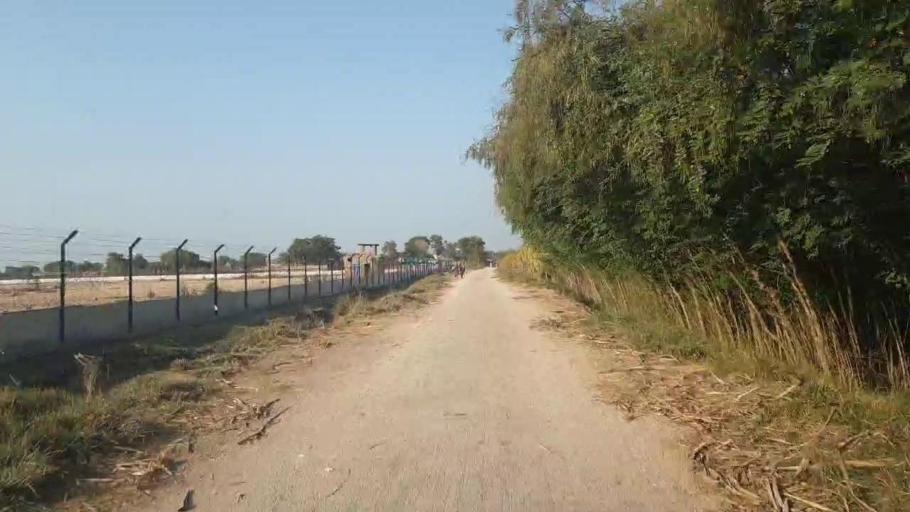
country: PK
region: Sindh
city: Bhit Shah
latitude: 25.8306
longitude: 68.5201
